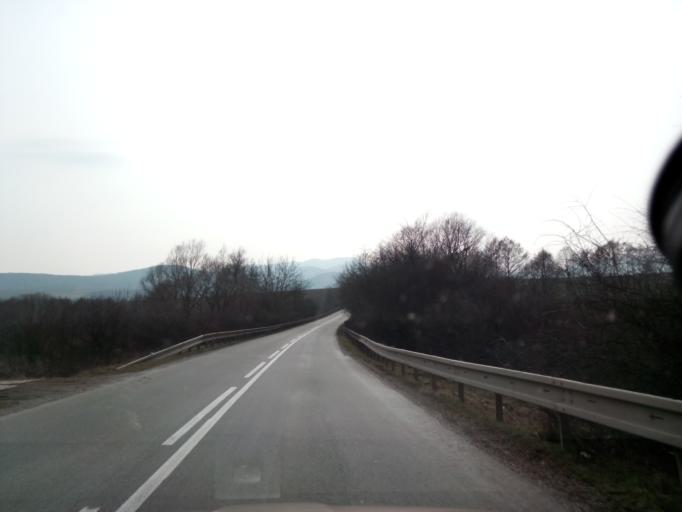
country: SK
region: Kosicky
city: Secovce
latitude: 48.6242
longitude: 21.5494
